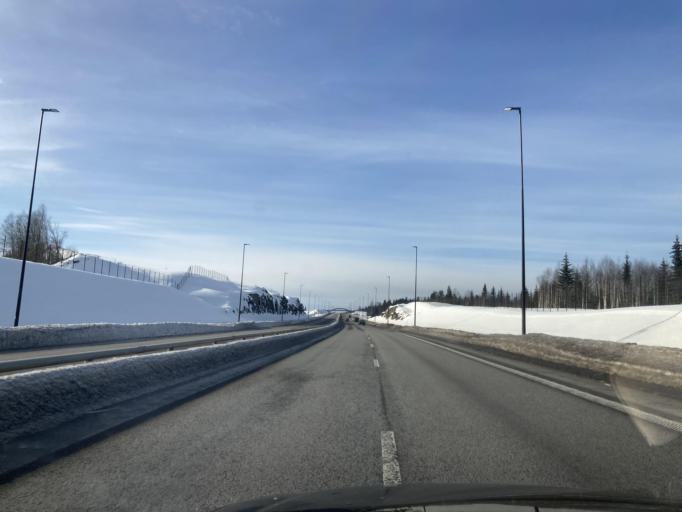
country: NO
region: Hedmark
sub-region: Elverum
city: Elverum
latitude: 60.8822
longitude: 11.4800
